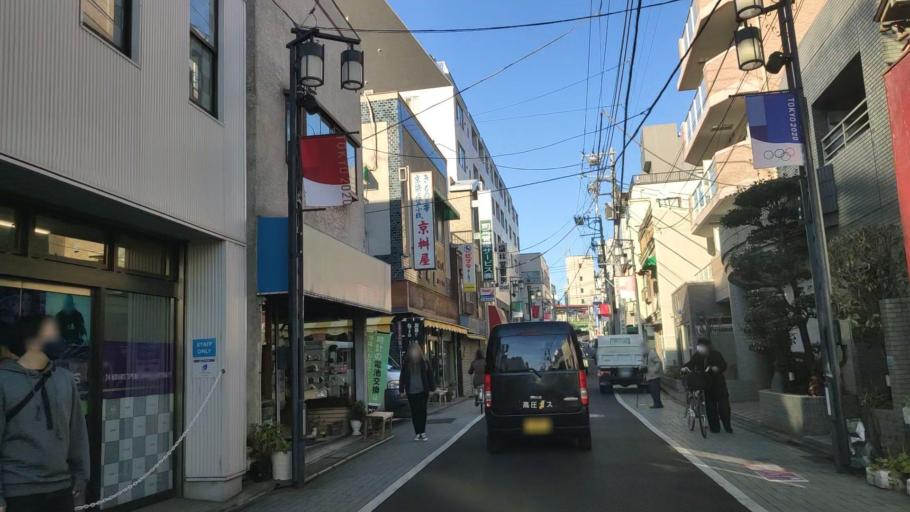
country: JP
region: Tokyo
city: Musashino
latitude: 35.7017
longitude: 139.5996
